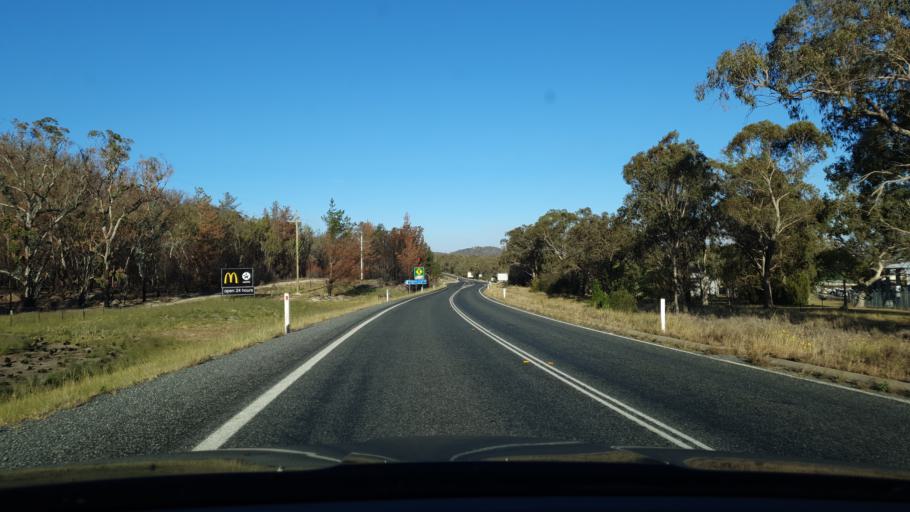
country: AU
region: Queensland
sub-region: Southern Downs
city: Stanthorpe
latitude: -28.6443
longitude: 151.9290
